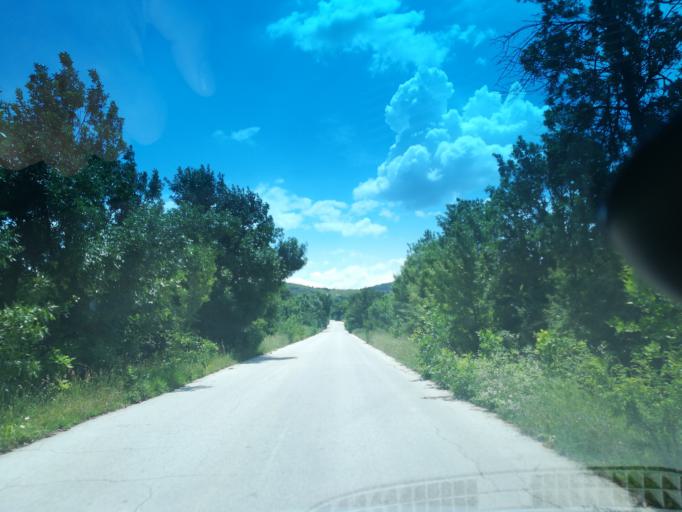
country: BG
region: Khaskovo
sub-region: Obshtina Mineralni Bani
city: Mineralni Bani
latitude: 41.9897
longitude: 25.2410
